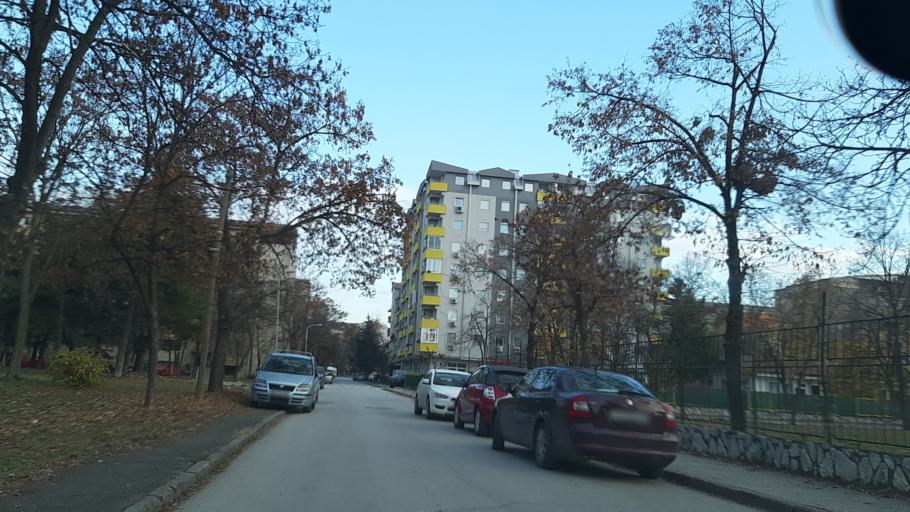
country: MK
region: Karpos
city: Skopje
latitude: 41.9808
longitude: 21.4457
